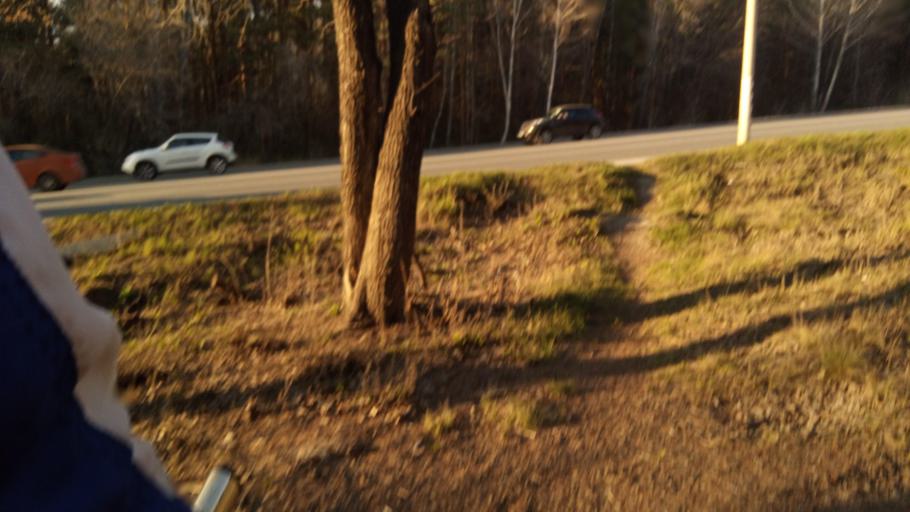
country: RU
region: Chelyabinsk
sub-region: Gorod Chelyabinsk
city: Chelyabinsk
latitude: 55.1465
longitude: 61.3444
